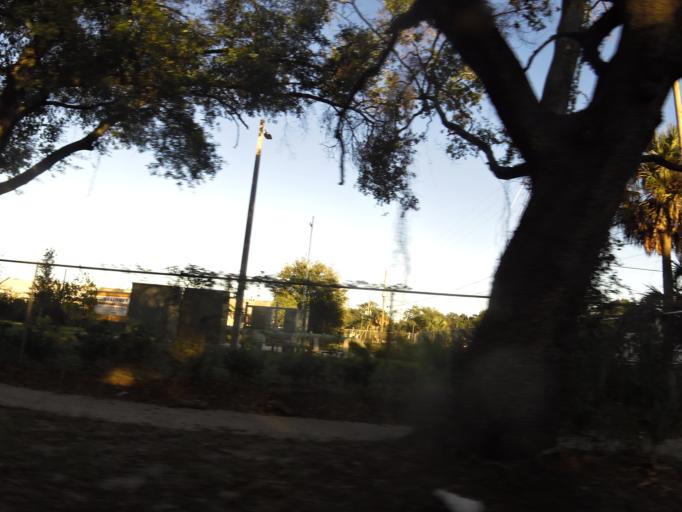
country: US
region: Florida
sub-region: Duval County
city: Jacksonville
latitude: 30.3346
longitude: -81.6473
